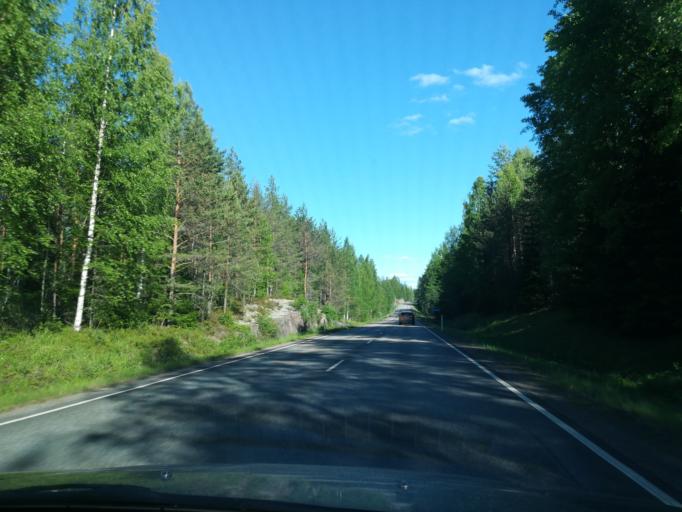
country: FI
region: South Karelia
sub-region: Imatra
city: Ruokolahti
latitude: 61.3649
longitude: 28.6900
